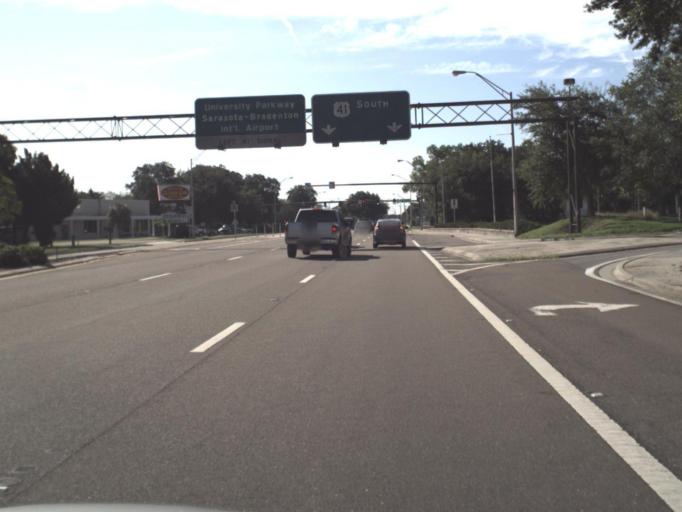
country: US
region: Florida
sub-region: Manatee County
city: Whitfield
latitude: 27.3834
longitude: -82.5575
